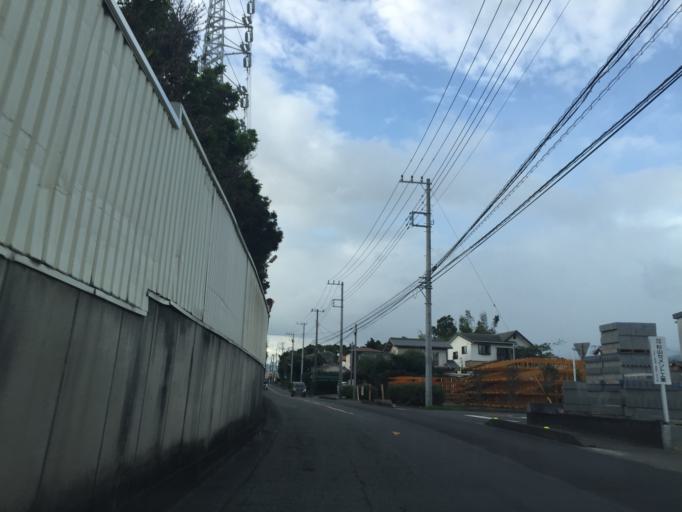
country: JP
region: Shizuoka
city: Mishima
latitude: 35.1596
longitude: 138.9104
